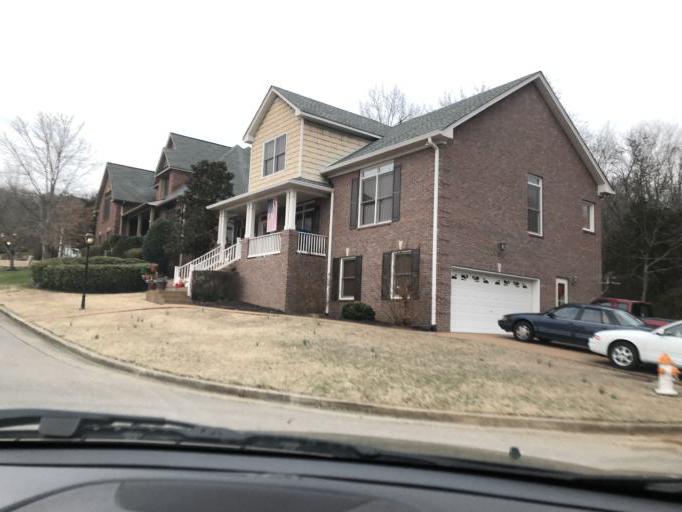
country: US
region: Tennessee
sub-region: Wilson County
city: Green Hill
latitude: 36.1952
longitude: -86.5896
